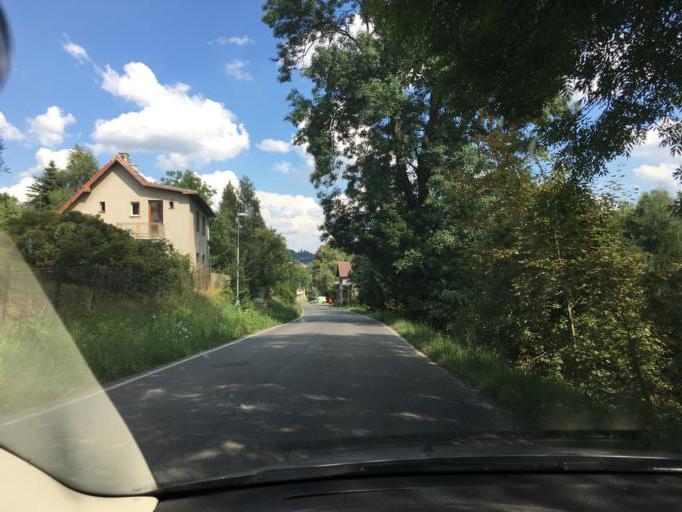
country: CZ
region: Liberecky
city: Semily
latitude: 50.6079
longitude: 15.3147
